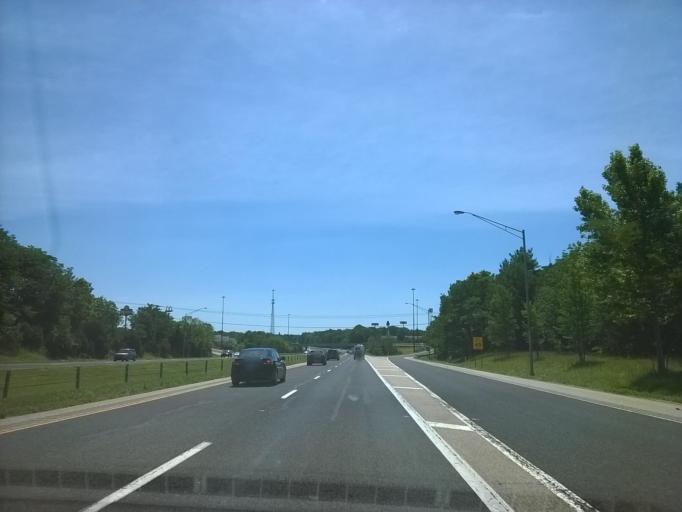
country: US
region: Indiana
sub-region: Ripley County
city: Batesville
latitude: 39.3104
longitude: -85.2209
